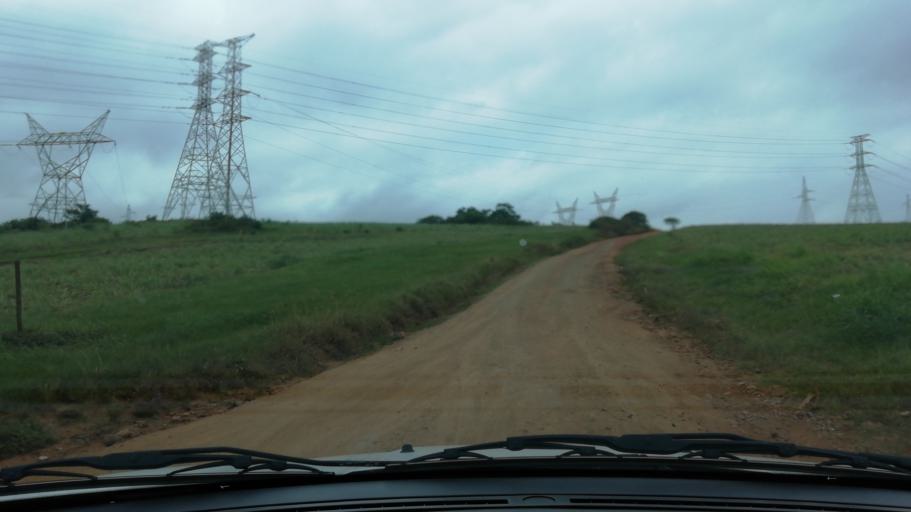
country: ZA
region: KwaZulu-Natal
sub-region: uThungulu District Municipality
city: Empangeni
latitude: -28.7327
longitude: 31.8997
